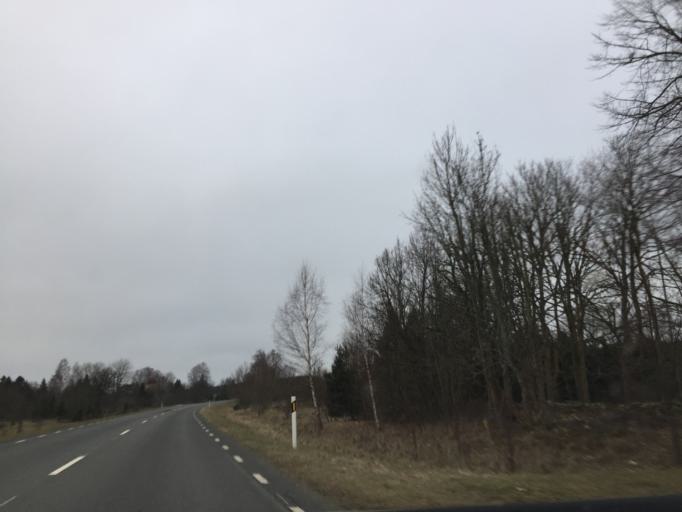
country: EE
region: Saare
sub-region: Kuressaare linn
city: Kuressaare
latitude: 58.5379
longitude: 22.3382
